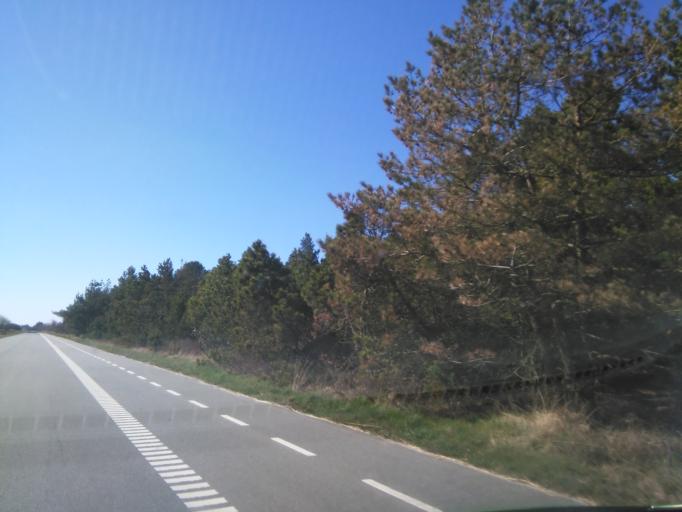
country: DK
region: South Denmark
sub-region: Varde Kommune
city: Oksbol
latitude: 55.5508
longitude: 8.1995
